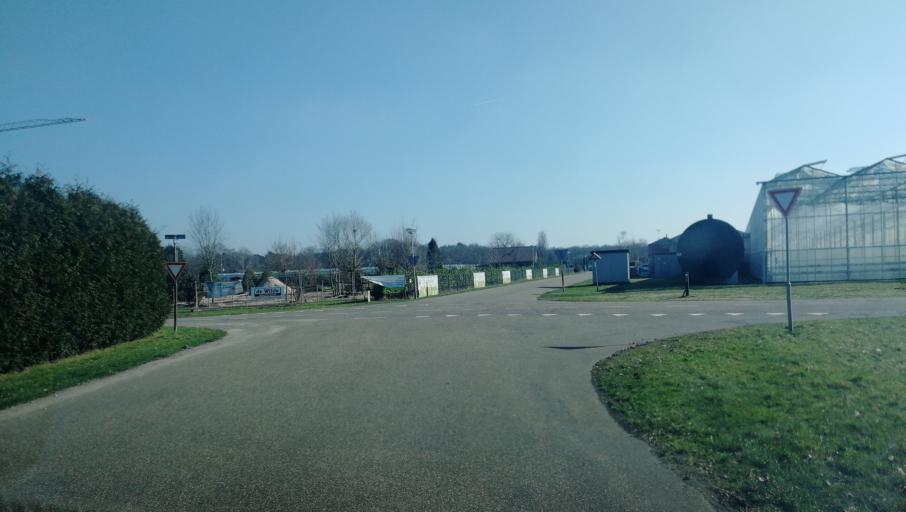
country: NL
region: Limburg
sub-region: Gemeente Venlo
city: Venlo
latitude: 51.3530
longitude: 6.1944
